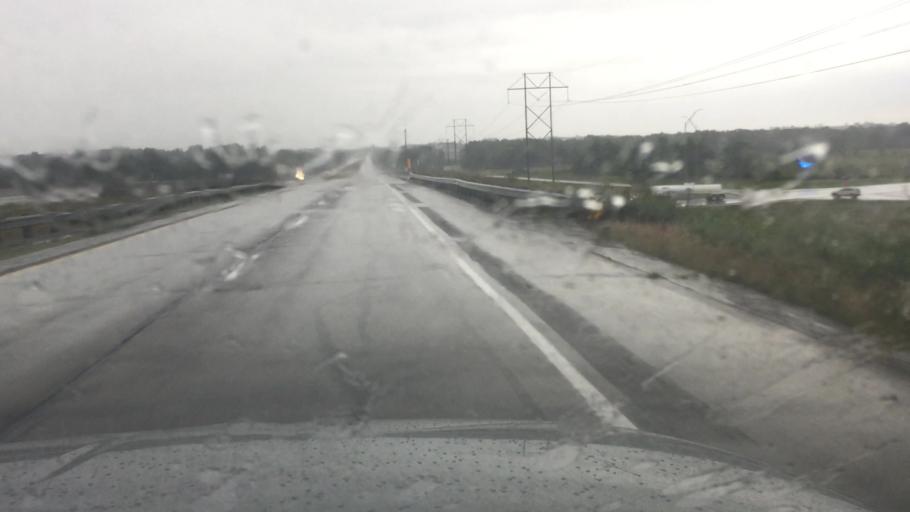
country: US
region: Iowa
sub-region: Johnson County
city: Lone Tree
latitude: 41.4880
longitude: -91.5518
